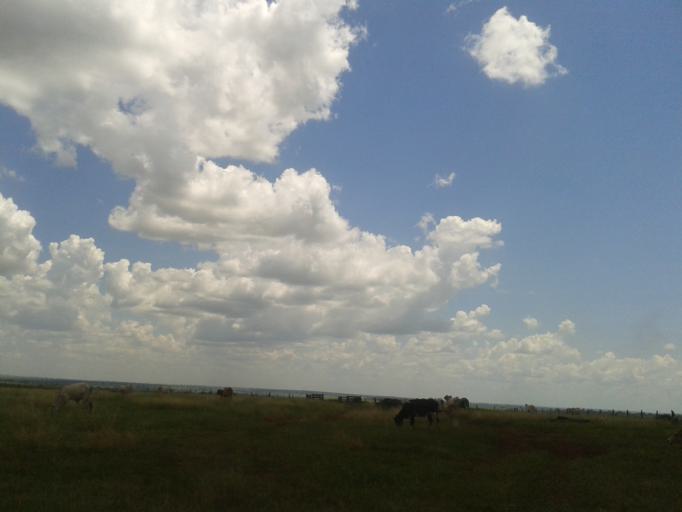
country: BR
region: Minas Gerais
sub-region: Santa Vitoria
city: Santa Vitoria
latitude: -19.1621
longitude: -50.4214
